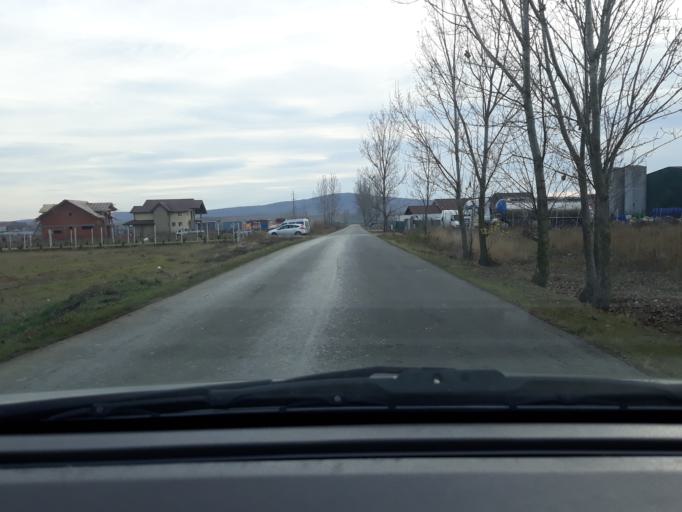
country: RO
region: Bihor
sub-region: Comuna Sanmartin
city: Sanmartin
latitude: 47.0246
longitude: 22.0039
